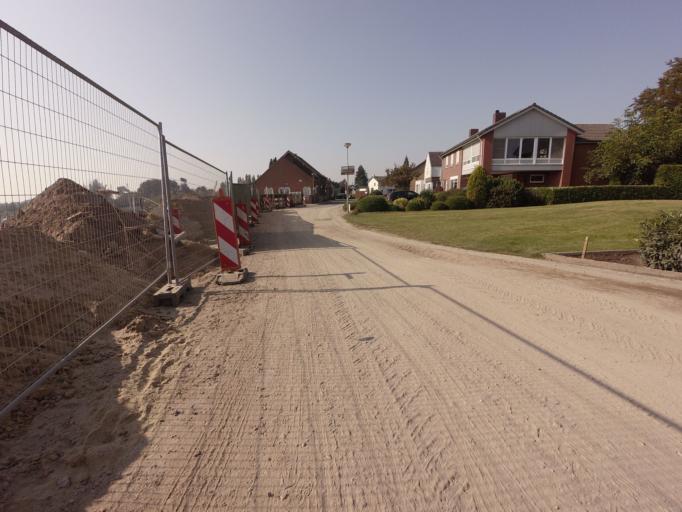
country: NL
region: Limburg
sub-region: Gemeente Beesel
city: Beesel
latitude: 51.2580
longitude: 6.0036
